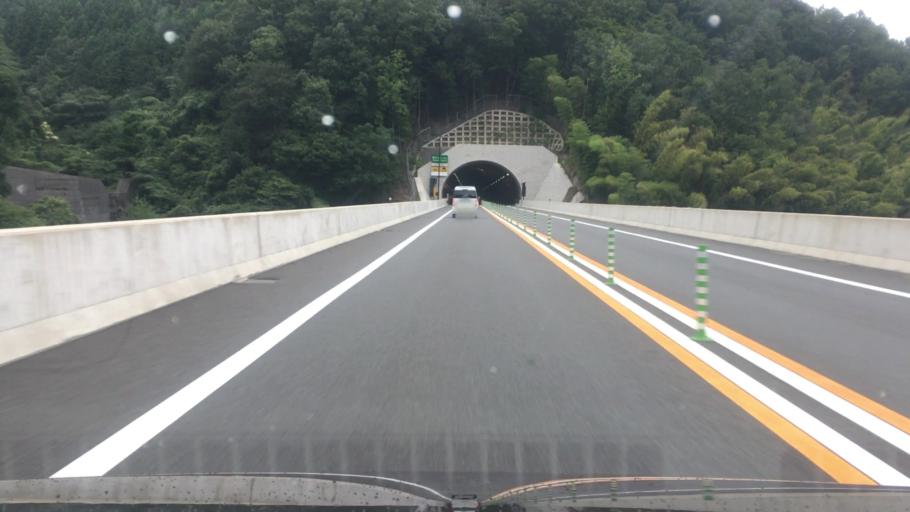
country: JP
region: Hyogo
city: Toyooka
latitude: 35.4493
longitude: 134.7657
